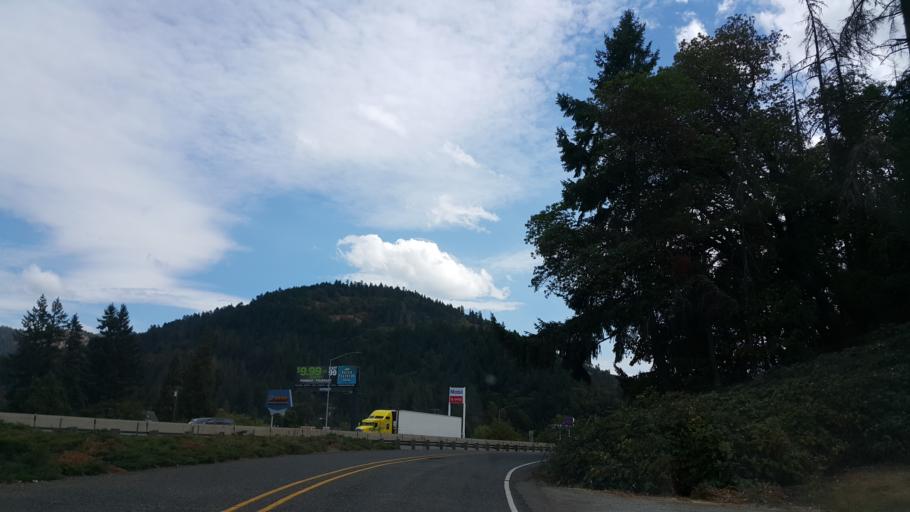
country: US
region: Oregon
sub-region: Douglas County
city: Canyonville
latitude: 42.9263
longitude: -123.2811
